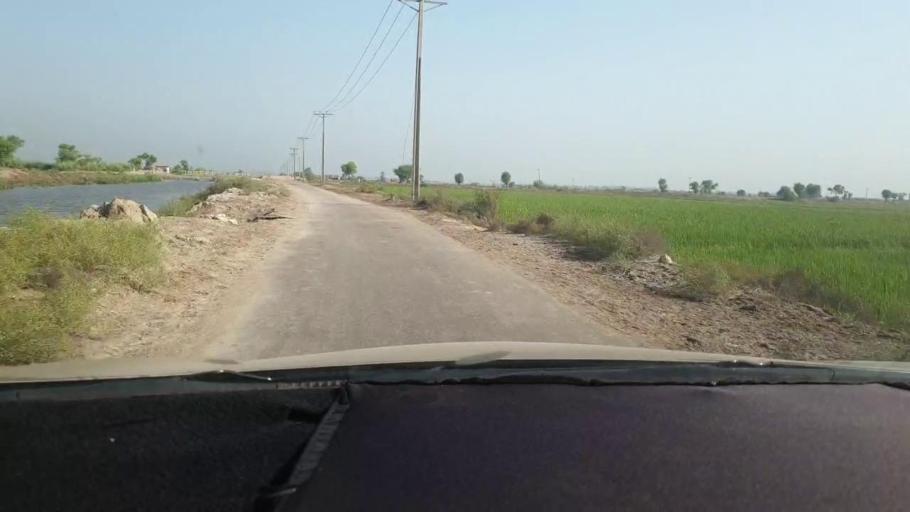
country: PK
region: Sindh
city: Miro Khan
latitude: 27.7618
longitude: 68.1337
